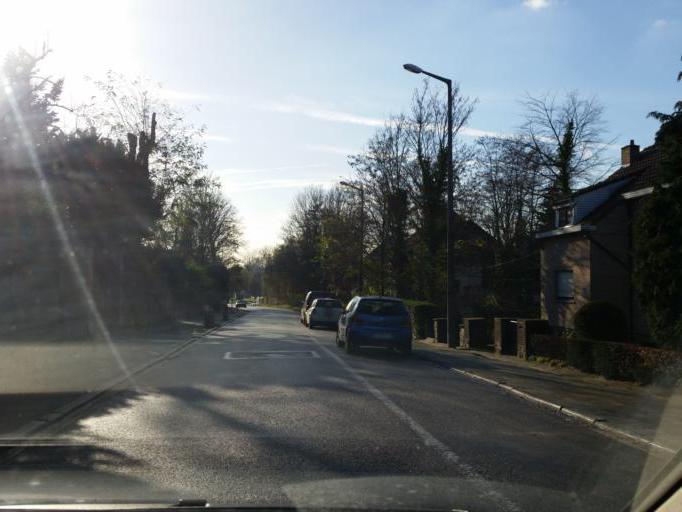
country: BE
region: Flanders
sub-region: Provincie Vlaams-Brabant
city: Diegem
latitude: 50.9046
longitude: 4.4291
